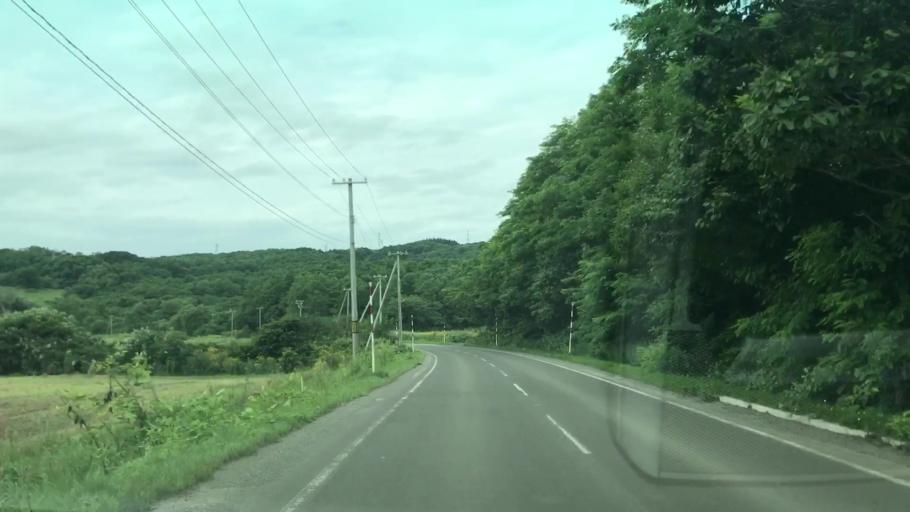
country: JP
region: Hokkaido
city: Iwanai
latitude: 43.0363
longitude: 140.5483
